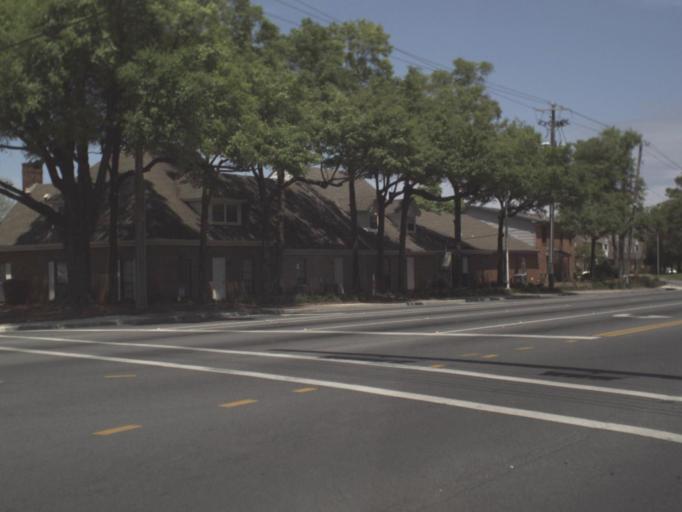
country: US
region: Florida
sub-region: Escambia County
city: Goulding
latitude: 30.4654
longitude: -87.2039
